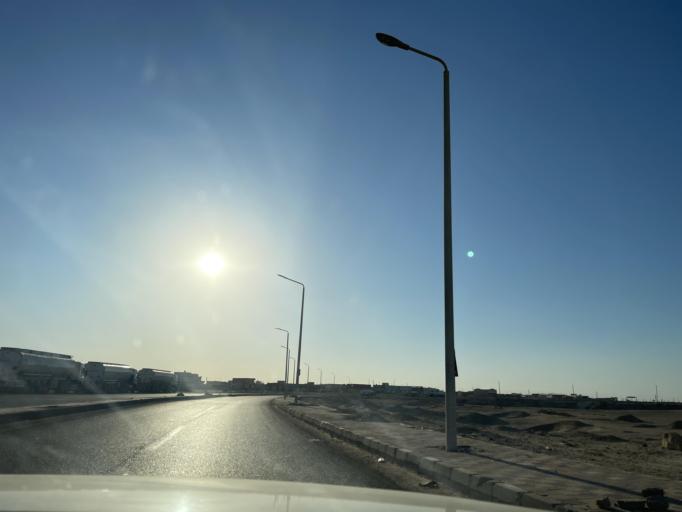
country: EG
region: Red Sea
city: Hurghada
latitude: 27.2192
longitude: 33.7876
